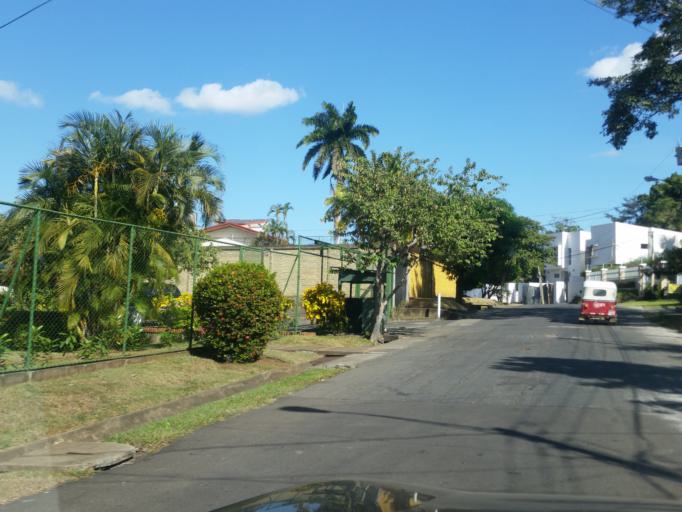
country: NI
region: Managua
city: Managua
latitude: 12.0929
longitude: -86.2407
